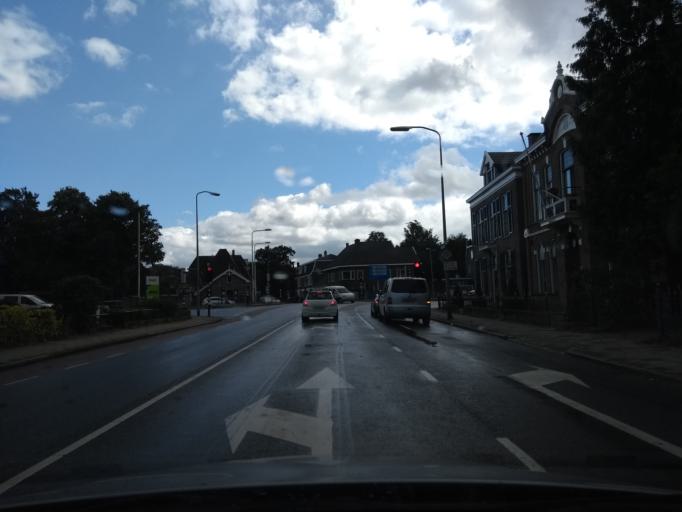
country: NL
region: Overijssel
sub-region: Gemeente Almelo
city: Almelo
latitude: 52.3627
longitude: 6.6682
